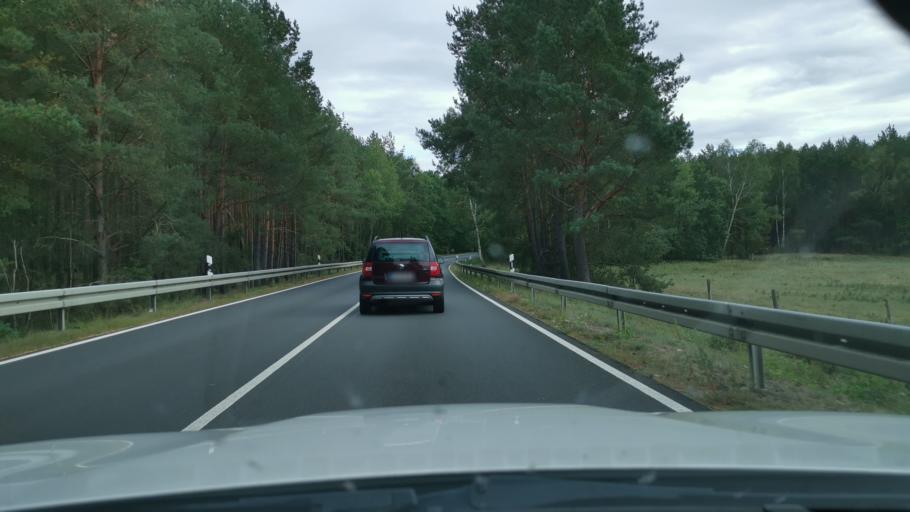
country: DE
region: Brandenburg
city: Wittstock
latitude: 53.1009
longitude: 12.4837
